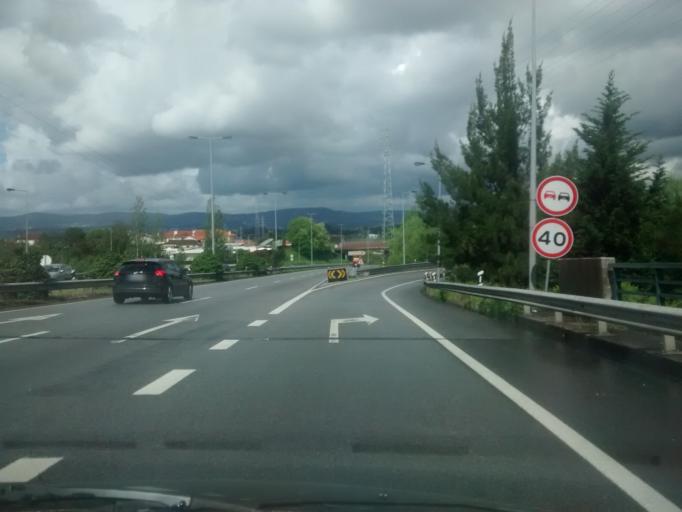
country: PT
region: Braga
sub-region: Braga
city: Braga
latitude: 41.5711
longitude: -8.4262
